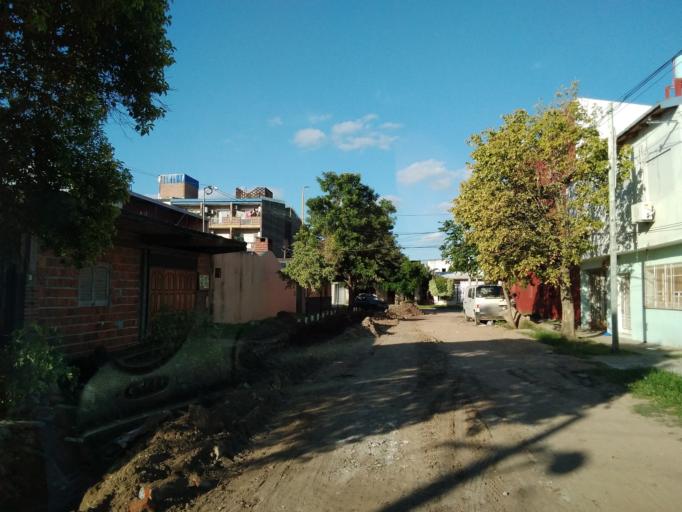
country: AR
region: Corrientes
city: Corrientes
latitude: -27.4630
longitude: -58.7852
